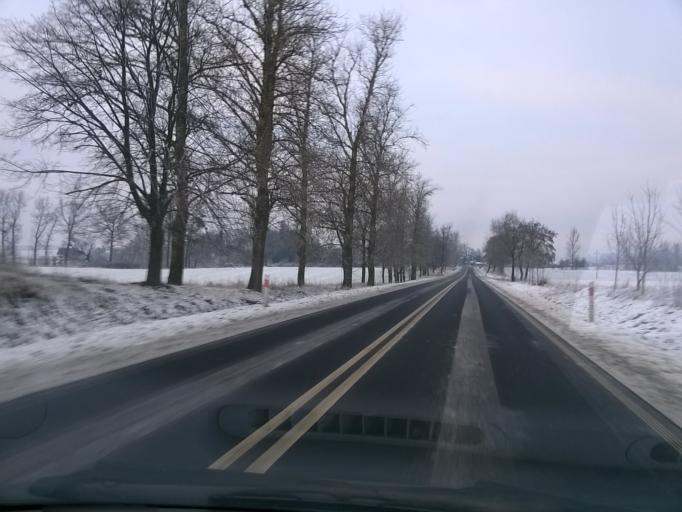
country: PL
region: Kujawsko-Pomorskie
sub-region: Powiat nakielski
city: Mrocza
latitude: 53.1934
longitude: 17.5806
